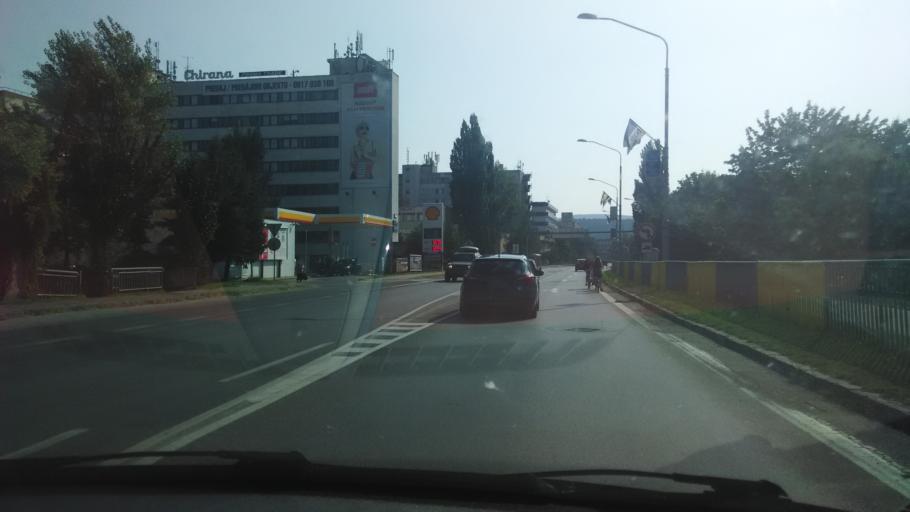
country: SK
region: Trnavsky
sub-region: Okres Trnava
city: Piestany
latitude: 48.5878
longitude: 17.8186
